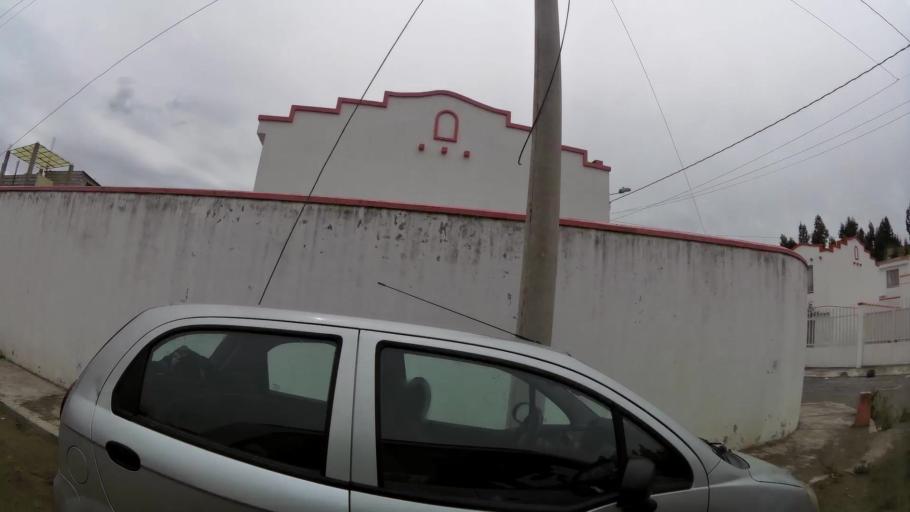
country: EC
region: Cotopaxi
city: Latacunga
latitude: -0.9416
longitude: -78.6080
